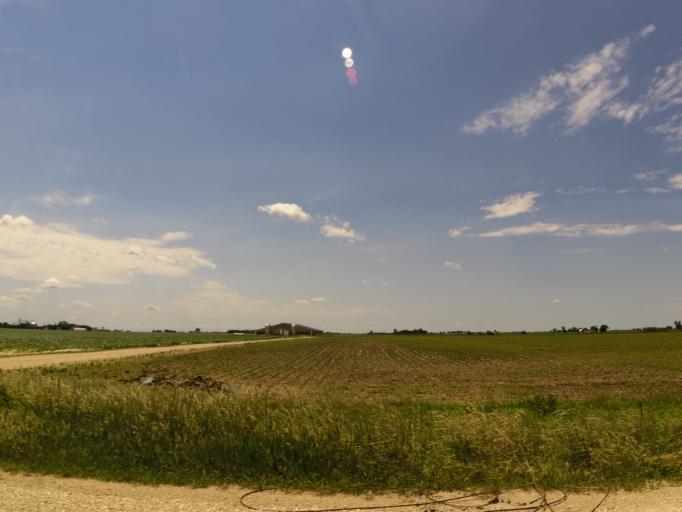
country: US
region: Iowa
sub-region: Buchanan County
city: Fairbank
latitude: 42.7146
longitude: -92.0919
